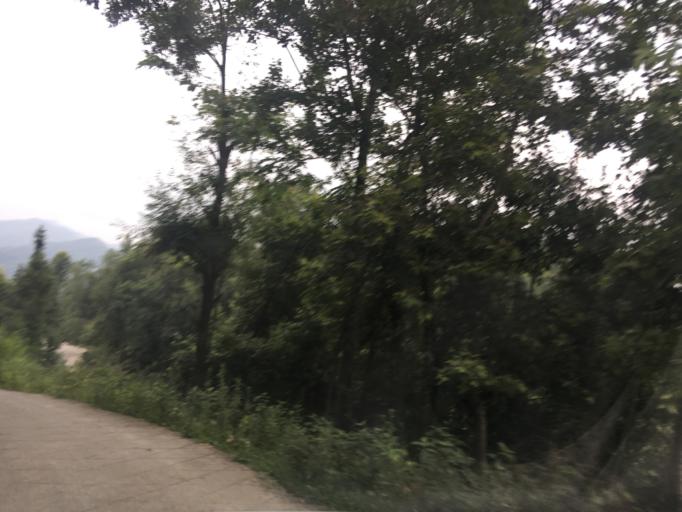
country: CN
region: Guangxi Zhuangzu Zizhiqu
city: Xinzhou
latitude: 25.1575
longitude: 105.6983
